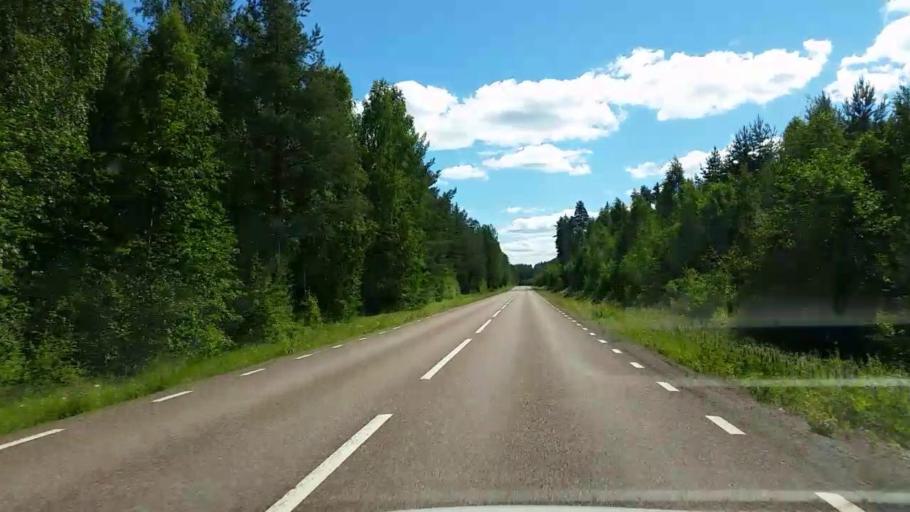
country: SE
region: Dalarna
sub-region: Faluns Kommun
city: Svardsjo
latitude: 60.9678
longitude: 15.6920
